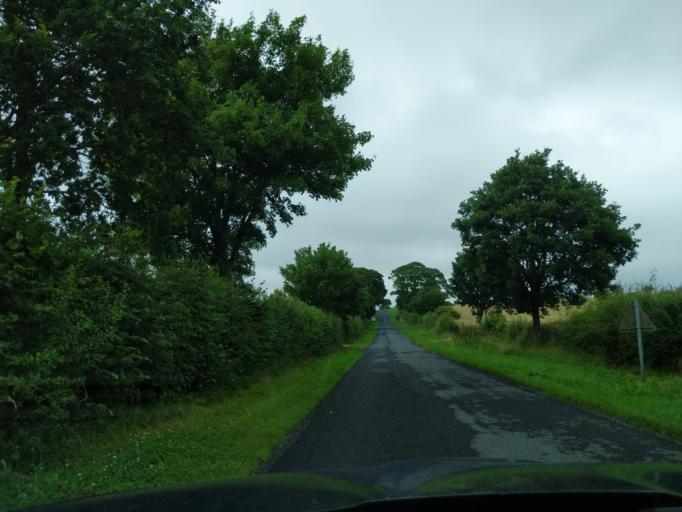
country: GB
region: England
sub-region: Northumberland
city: Ford
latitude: 55.6979
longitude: -2.1421
